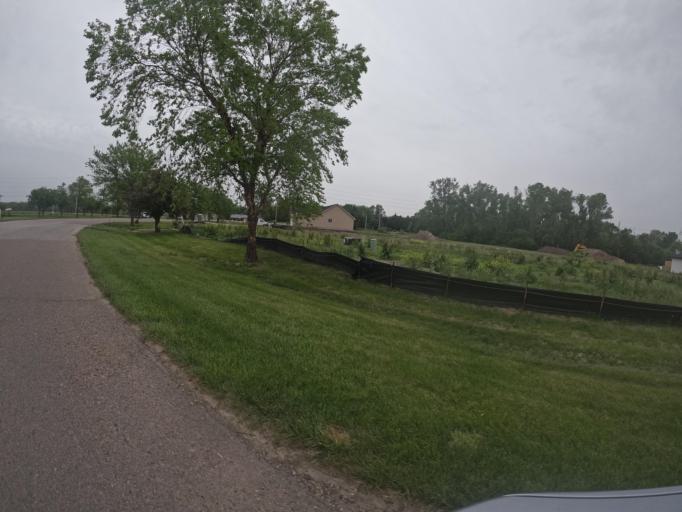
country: US
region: Nebraska
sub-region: Cass County
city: Plattsmouth
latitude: 41.0471
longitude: -95.9533
